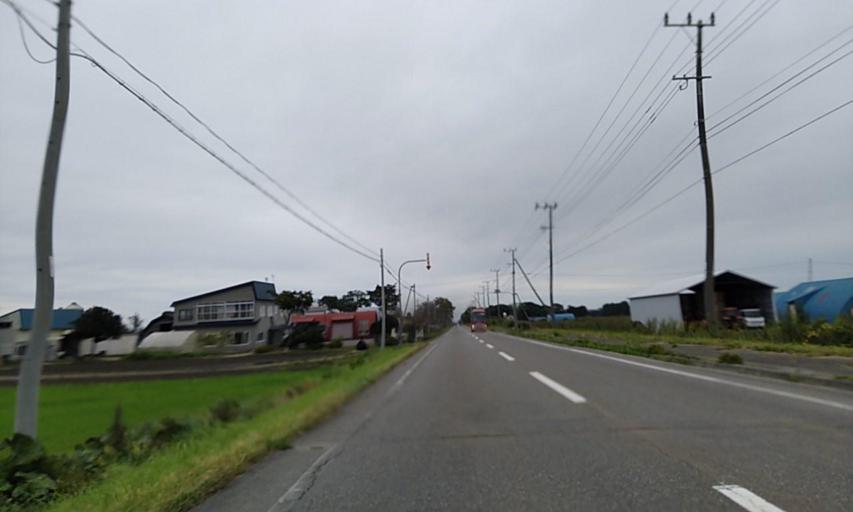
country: JP
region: Hokkaido
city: Obihiro
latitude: 42.6420
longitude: 143.0956
